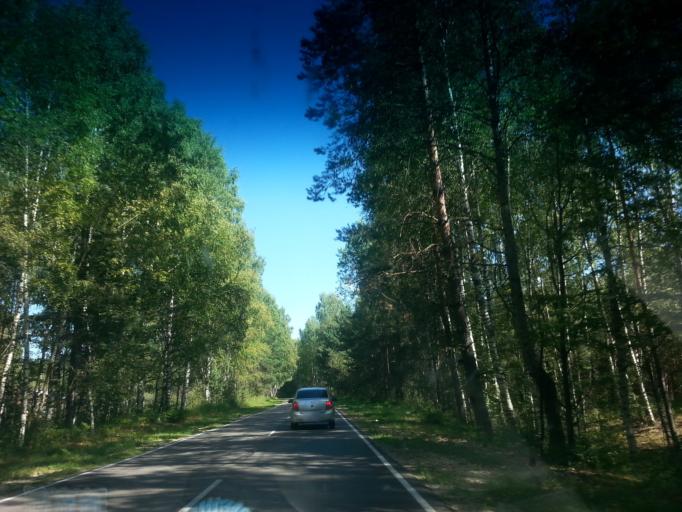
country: RU
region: Vladimir
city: Galitsy
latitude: 55.9986
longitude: 42.8704
